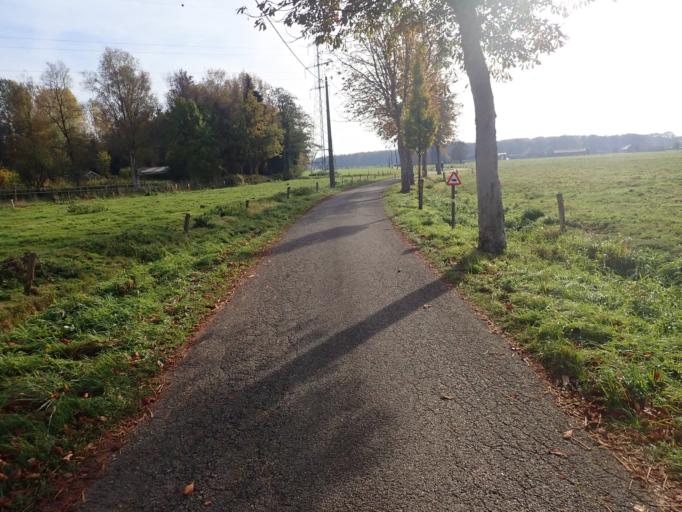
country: BE
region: Flanders
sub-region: Provincie Antwerpen
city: Zoersel
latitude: 51.2667
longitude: 4.7201
